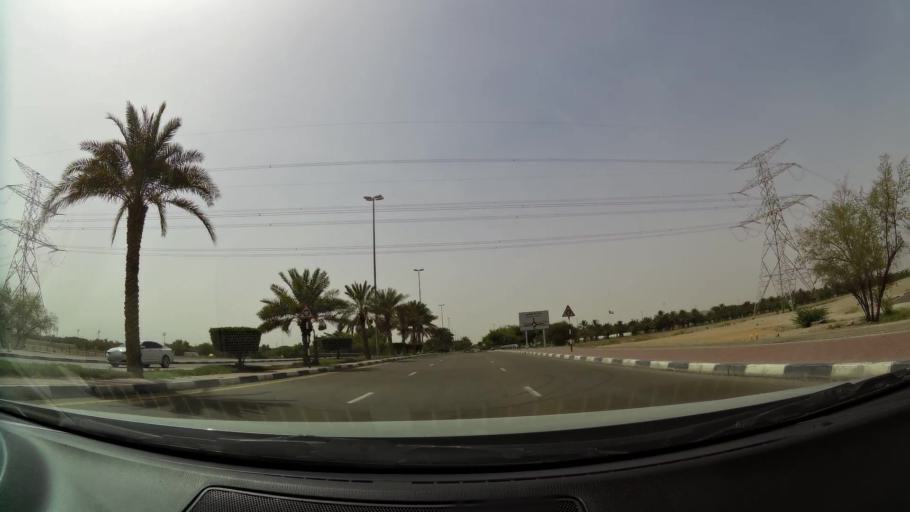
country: AE
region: Abu Dhabi
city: Al Ain
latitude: 24.1735
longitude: 55.6652
